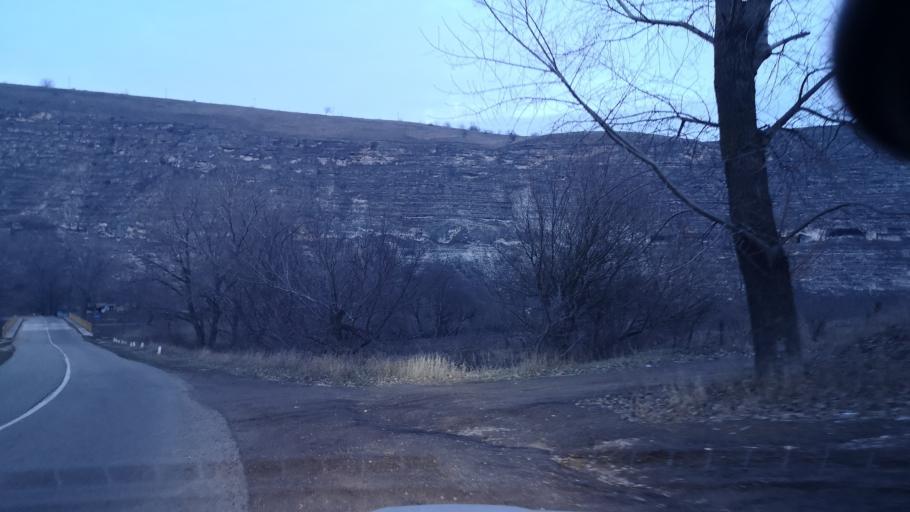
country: MD
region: Telenesti
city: Cocieri
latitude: 47.3075
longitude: 28.9877
